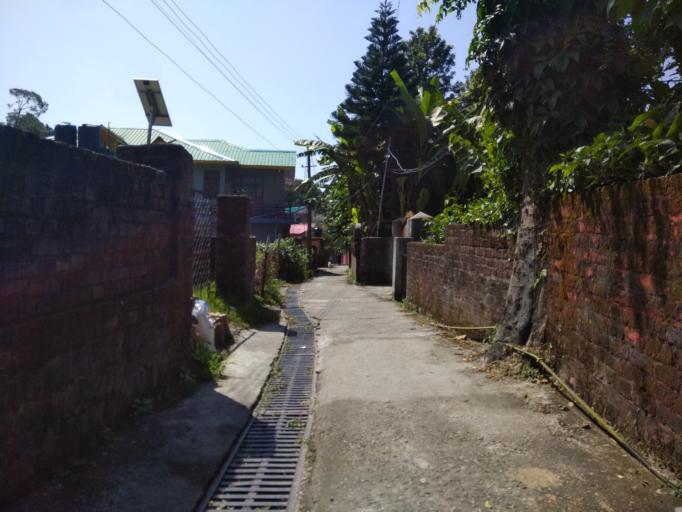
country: IN
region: Himachal Pradesh
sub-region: Kangra
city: Palampur
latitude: 32.1217
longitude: 76.5396
